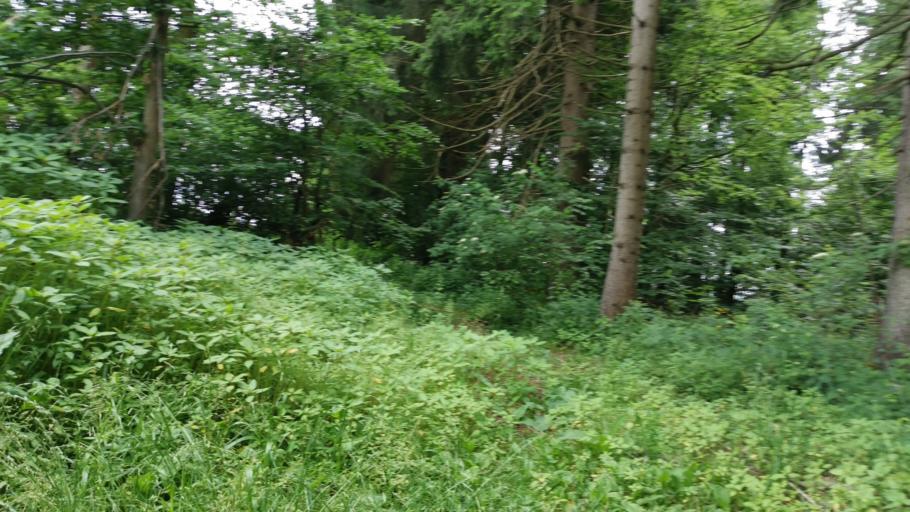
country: DE
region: Bavaria
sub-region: Upper Bavaria
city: Schaftlarn
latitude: 48.0058
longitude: 11.4592
